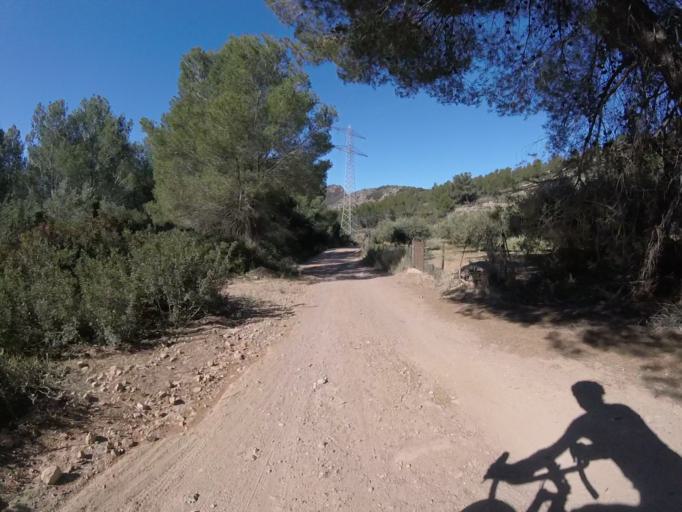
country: ES
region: Valencia
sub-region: Provincia de Castello
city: Benicassim
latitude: 40.0811
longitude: 0.0833
